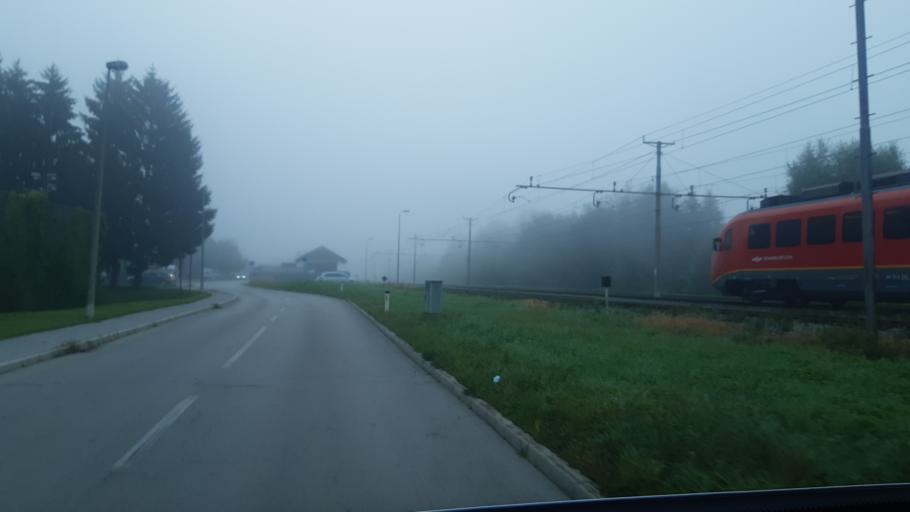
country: SI
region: Medvode
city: Medvode
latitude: 46.1393
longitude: 14.4090
